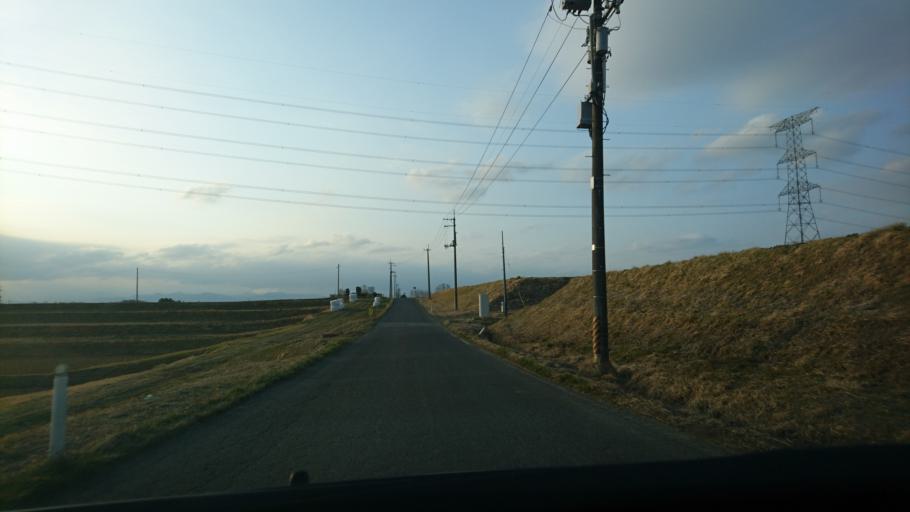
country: JP
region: Iwate
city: Ichinoseki
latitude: 38.8846
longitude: 141.1958
